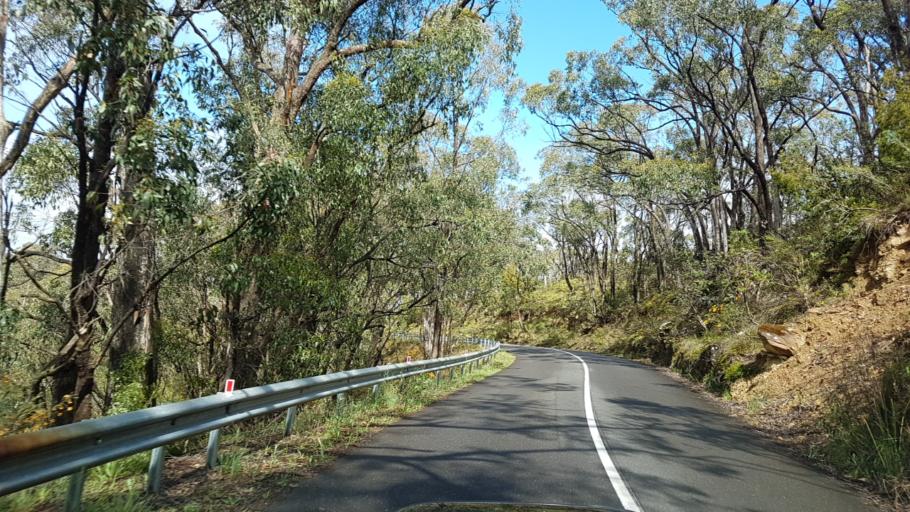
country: AU
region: South Australia
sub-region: Adelaide Hills
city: Adelaide Hills
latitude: -34.9138
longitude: 138.7569
